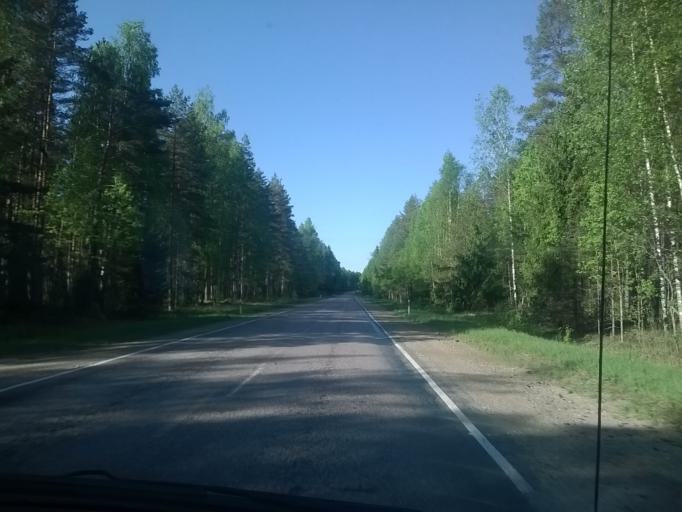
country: LV
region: Strenci
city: Seda
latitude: 57.6431
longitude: 25.8393
